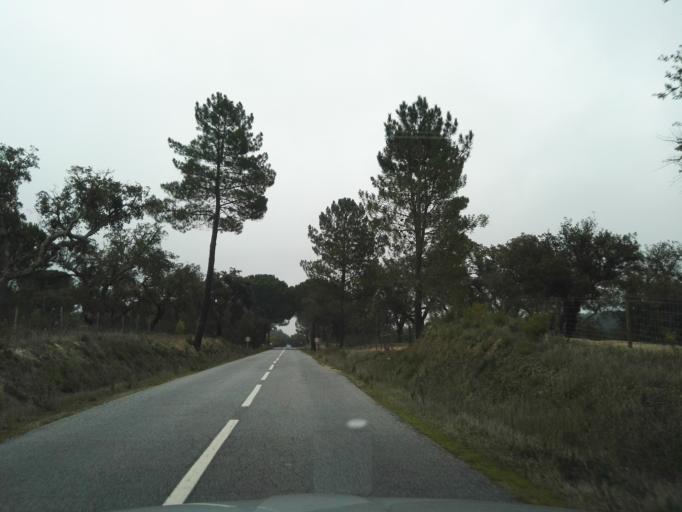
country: PT
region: Evora
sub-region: Vendas Novas
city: Vendas Novas
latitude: 38.7647
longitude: -8.4112
